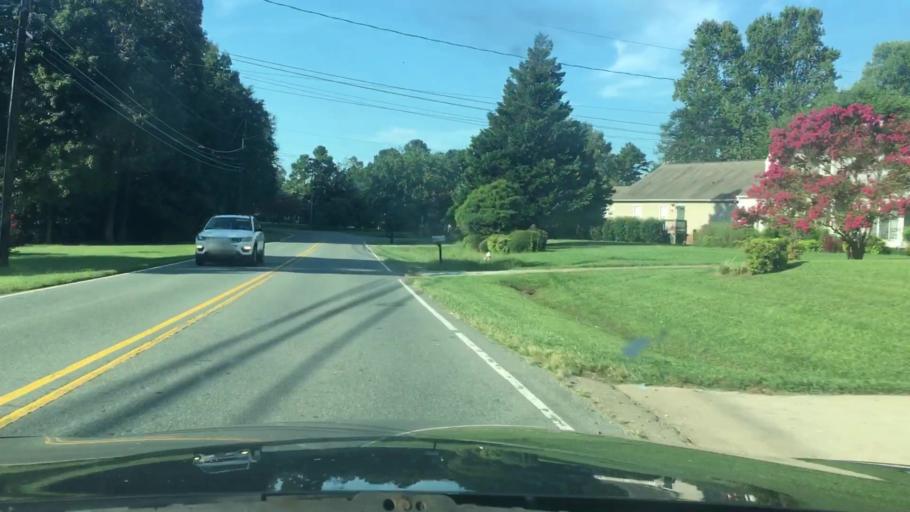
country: US
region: North Carolina
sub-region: Alamance County
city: Elon
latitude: 36.0914
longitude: -79.5114
